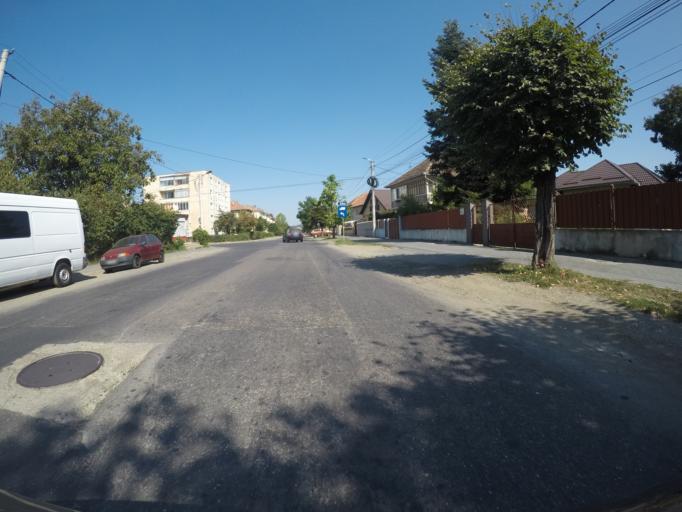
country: RO
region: Brasov
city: Fogarasch
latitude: 45.8322
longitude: 24.9763
